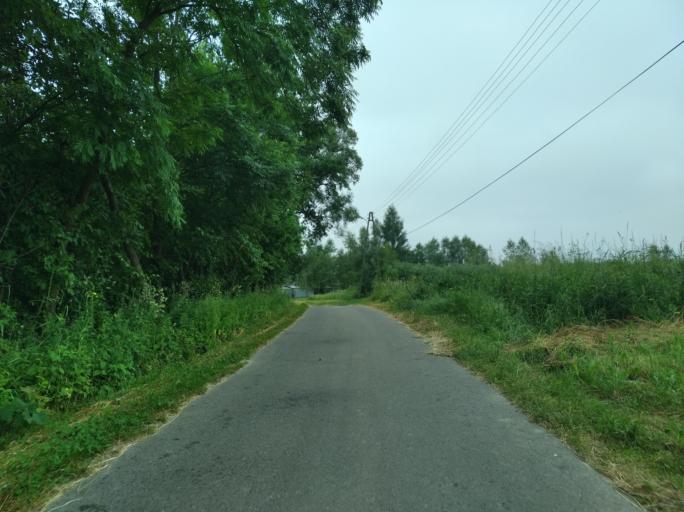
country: PL
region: Subcarpathian Voivodeship
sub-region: Powiat brzozowski
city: Jablonica Polska
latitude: 49.6913
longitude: 21.8871
